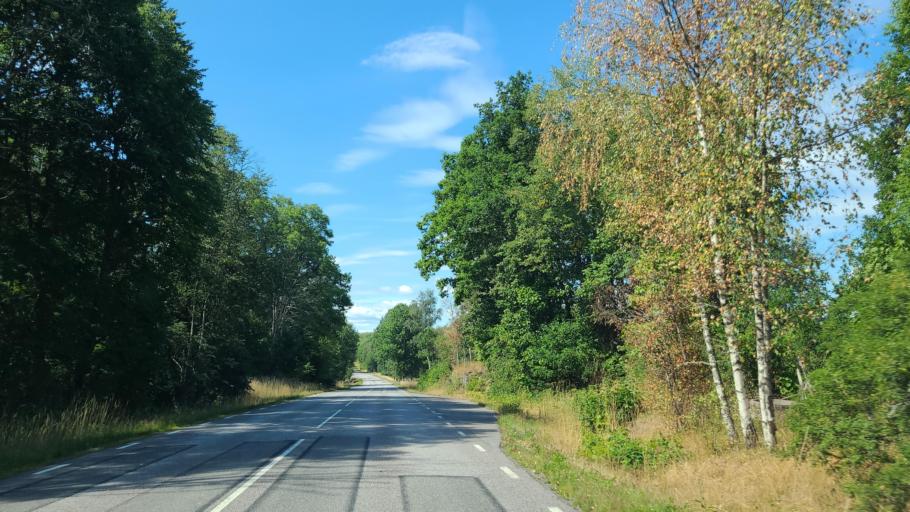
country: SE
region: Kalmar
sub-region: Emmaboda Kommun
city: Emmaboda
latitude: 56.5542
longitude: 15.7162
